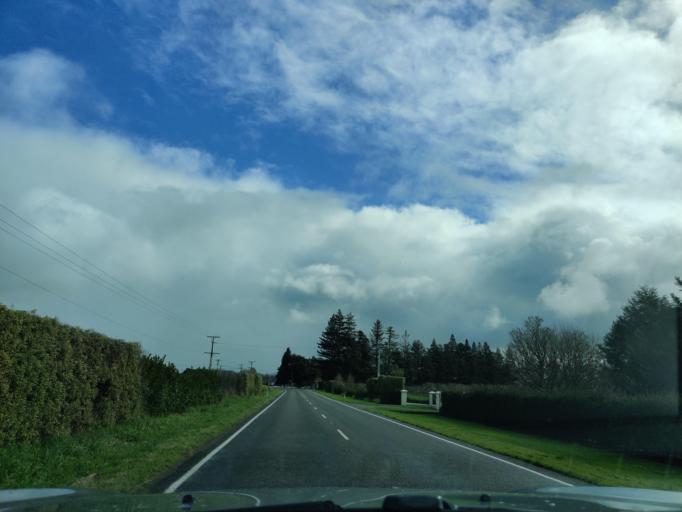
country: NZ
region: Hawke's Bay
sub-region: Hastings District
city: Hastings
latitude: -39.6783
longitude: 176.8511
